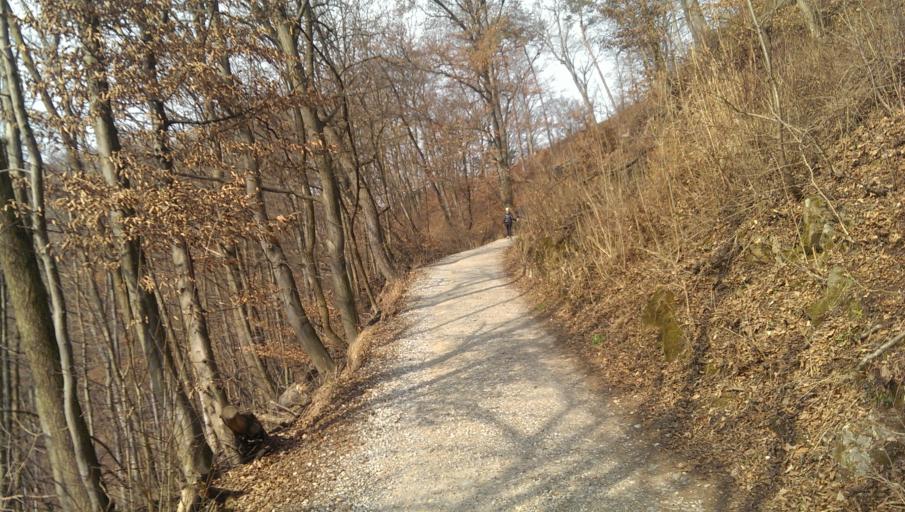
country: AT
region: Styria
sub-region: Graz Stadt
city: Goesting
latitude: 47.1036
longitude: 15.3850
